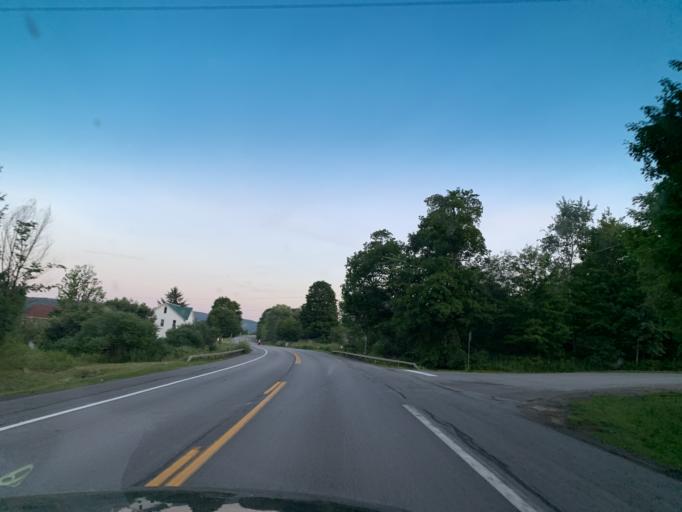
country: US
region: New York
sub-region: Oneida County
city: Waterville
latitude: 42.8333
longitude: -75.2555
